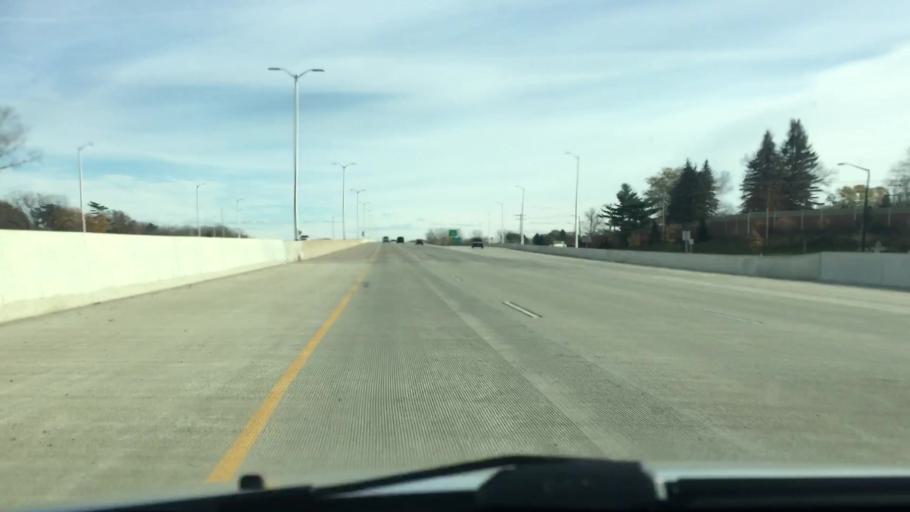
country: US
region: Wisconsin
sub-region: Brown County
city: Howard
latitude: 44.5458
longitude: -88.0954
